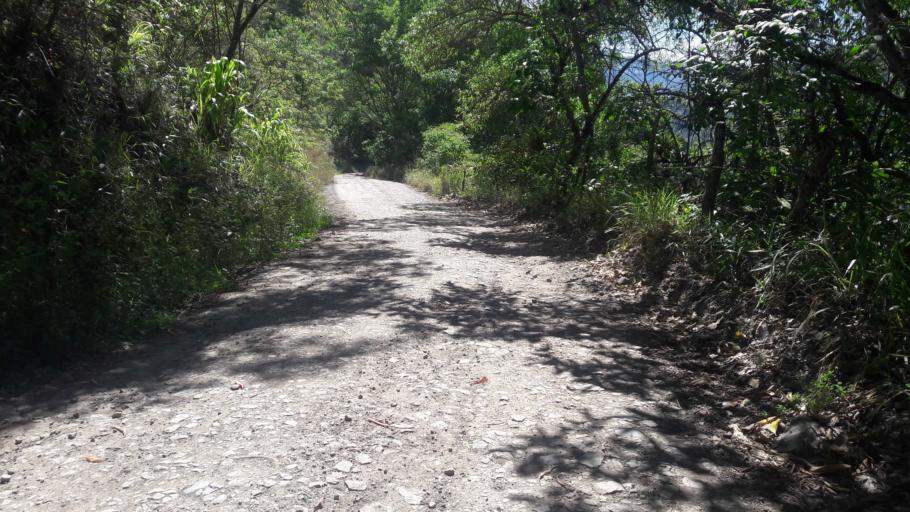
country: CO
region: Cundinamarca
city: Tenza
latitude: 5.0856
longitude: -73.4220
